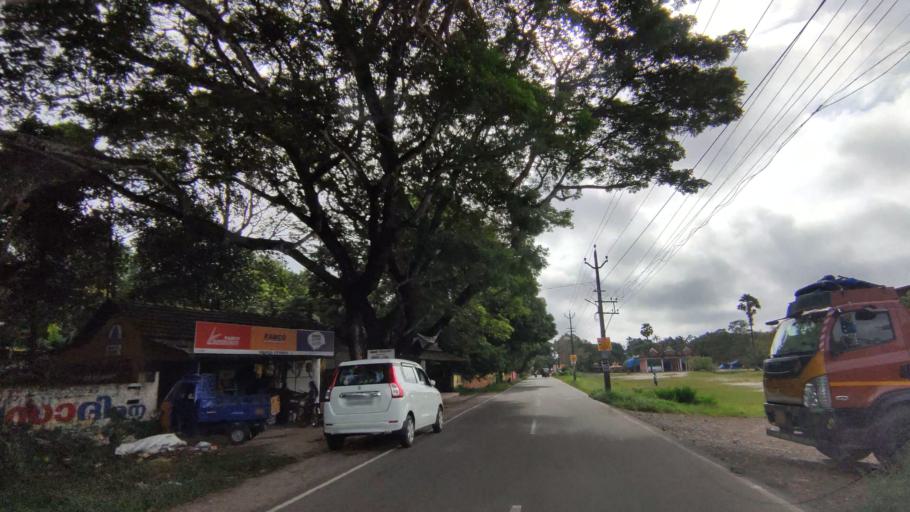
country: IN
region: Kerala
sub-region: Alappuzha
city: Shertallai
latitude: 9.6416
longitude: 76.3568
